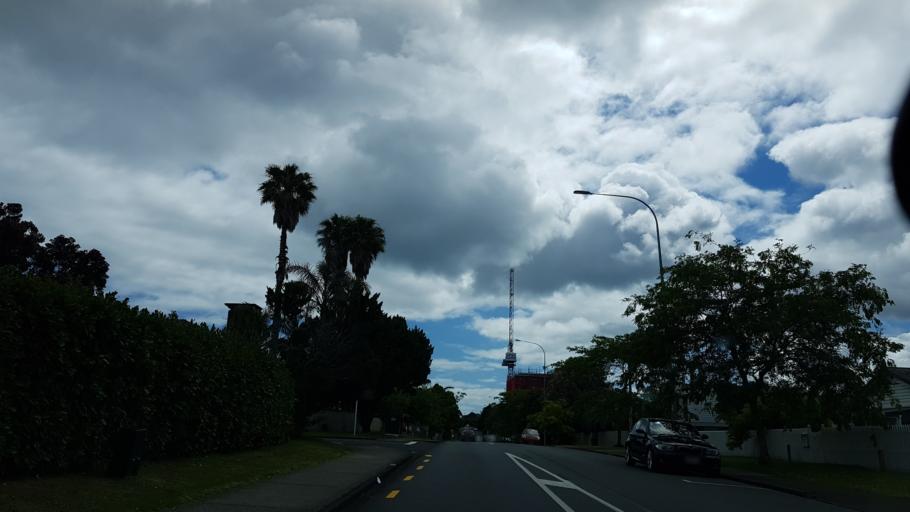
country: NZ
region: Auckland
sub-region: Auckland
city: North Shore
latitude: -36.7883
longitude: 174.7640
